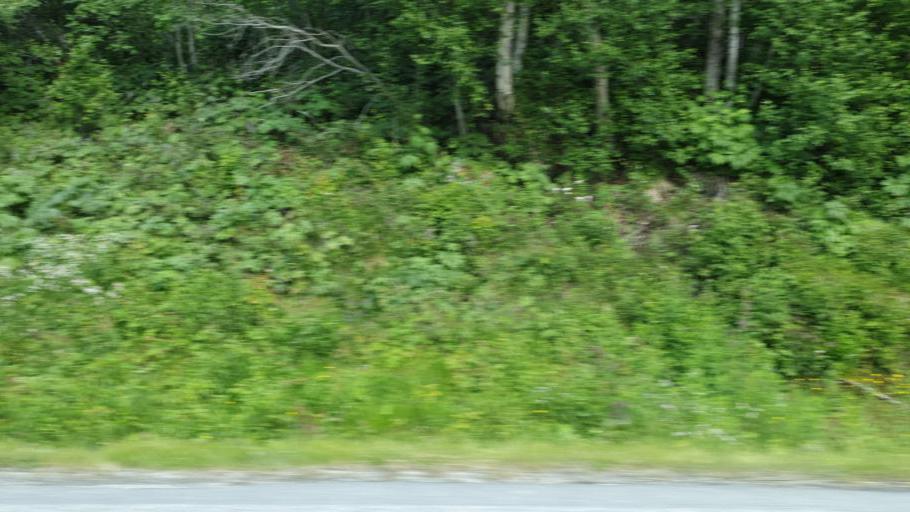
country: NO
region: Oppland
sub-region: Vaga
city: Vagamo
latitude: 61.8341
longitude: 8.9621
